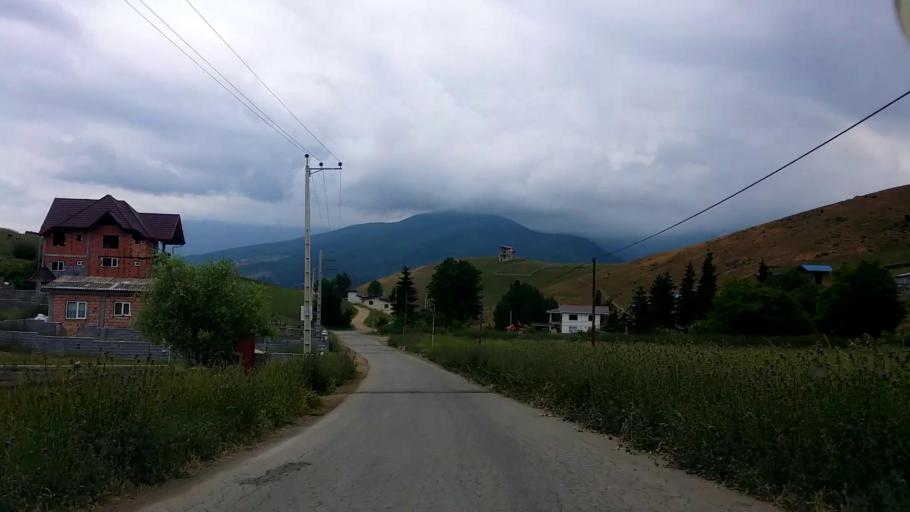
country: IR
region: Mazandaran
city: Chalus
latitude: 36.5230
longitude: 51.2622
